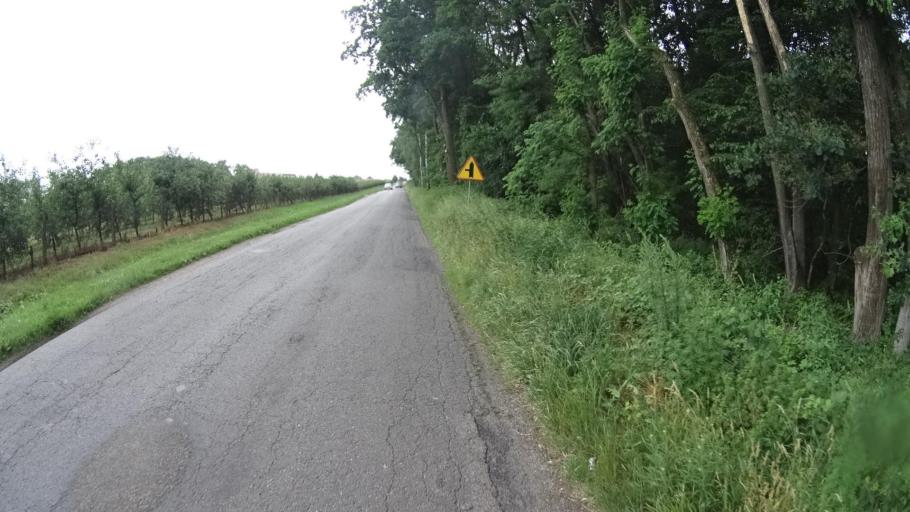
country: PL
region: Masovian Voivodeship
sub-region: Powiat grojecki
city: Goszczyn
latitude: 51.7777
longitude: 20.8535
